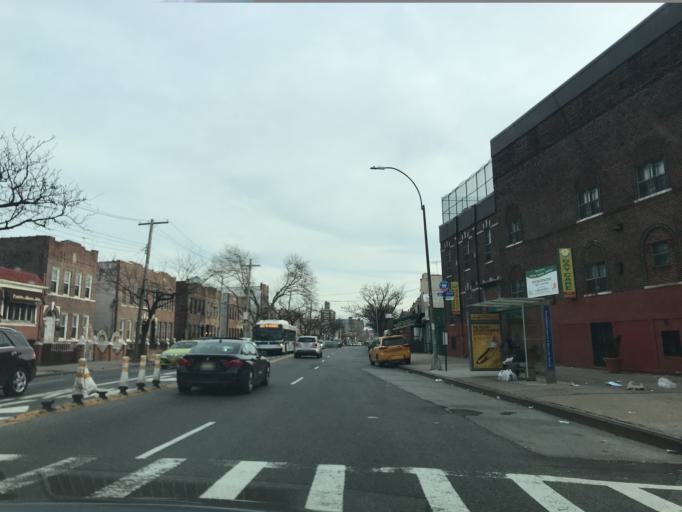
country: US
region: New York
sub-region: Kings County
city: East New York
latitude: 40.6619
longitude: -73.8931
